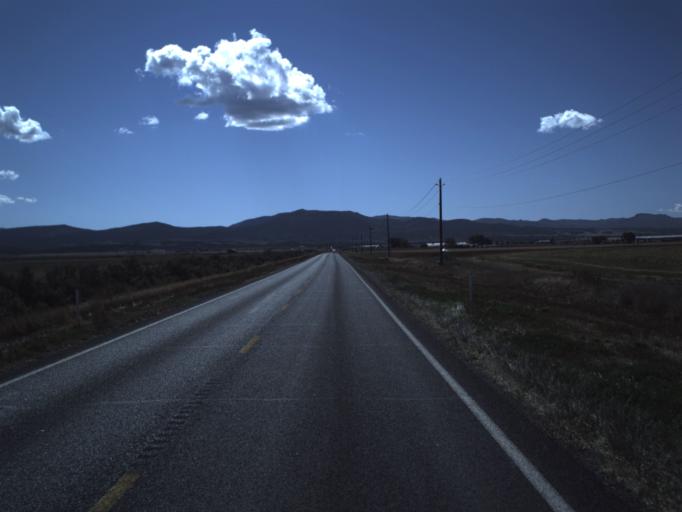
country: US
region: Utah
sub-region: Washington County
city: Enterprise
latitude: 37.6276
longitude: -113.6612
